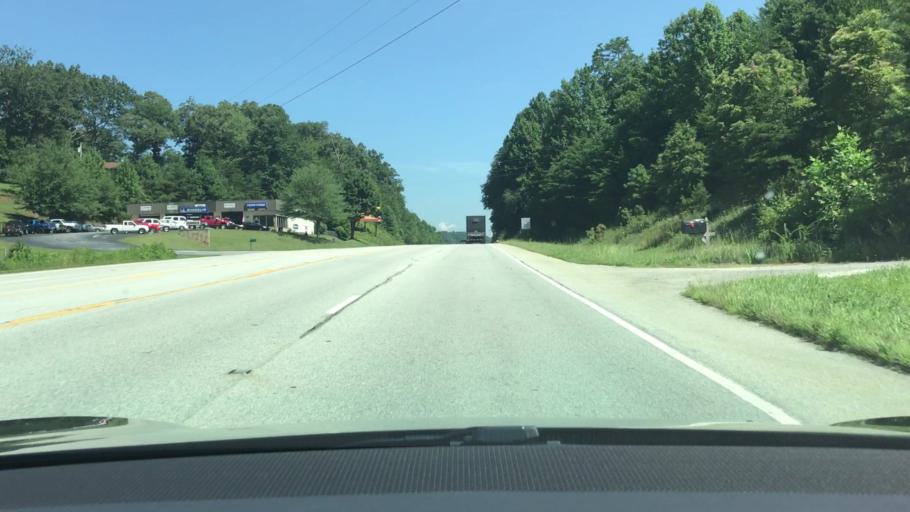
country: US
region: Georgia
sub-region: Rabun County
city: Mountain City
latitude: 35.0015
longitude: -83.3830
